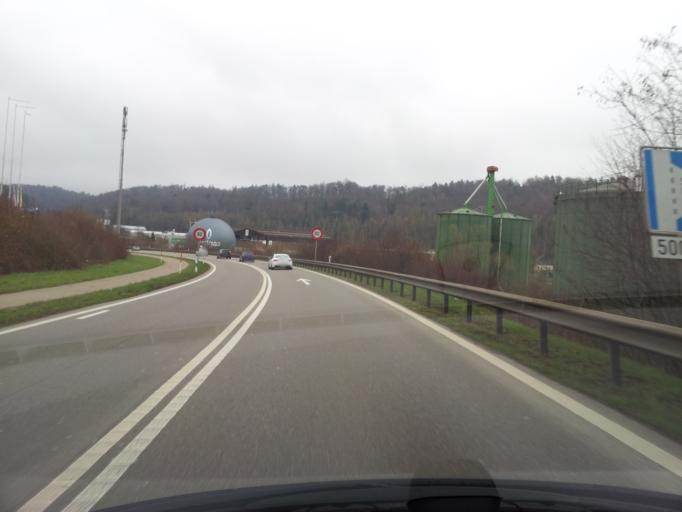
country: CH
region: Schaffhausen
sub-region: Bezirk Reiat
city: Stetten
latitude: 47.7189
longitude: 8.6648
